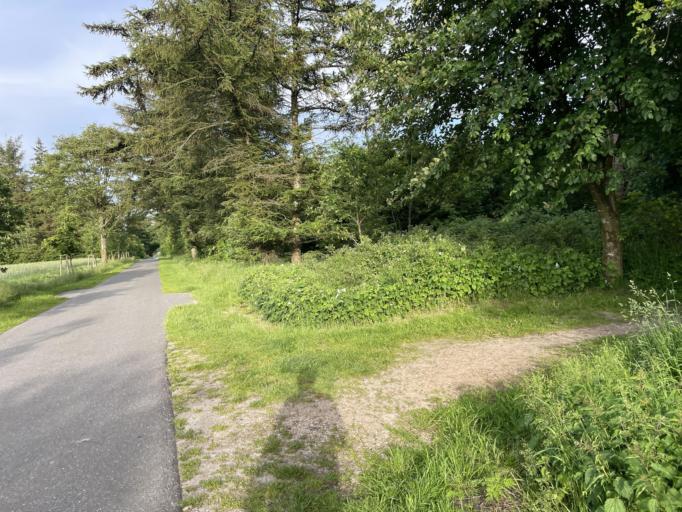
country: DE
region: Schleswig-Holstein
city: Mildstedt
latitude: 54.4659
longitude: 9.1077
